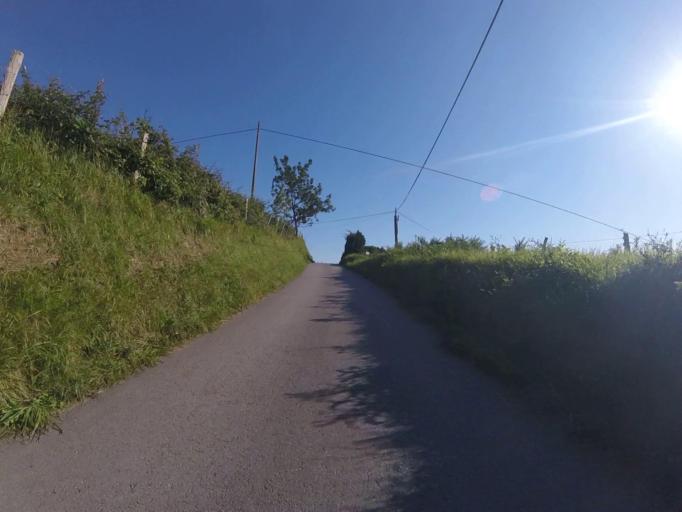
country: ES
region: Basque Country
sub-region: Provincia de Guipuzcoa
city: Fuenterrabia
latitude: 43.3767
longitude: -1.8111
